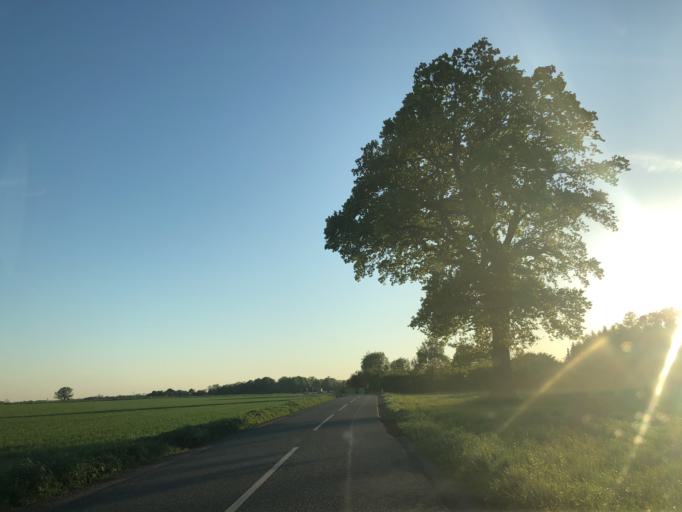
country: DK
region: Zealand
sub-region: Faxe Kommune
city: Haslev
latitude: 55.4111
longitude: 11.9034
